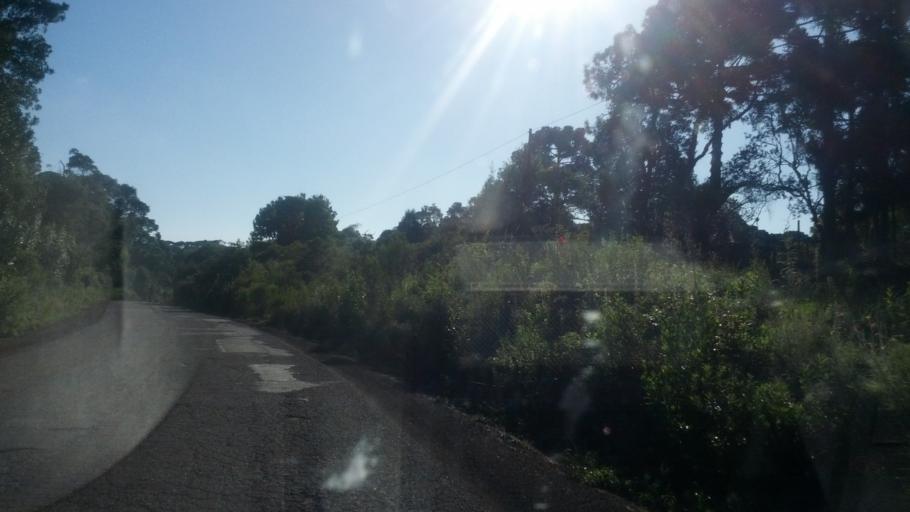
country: BR
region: Santa Catarina
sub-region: Lages
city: Lages
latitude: -27.9267
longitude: -50.5561
